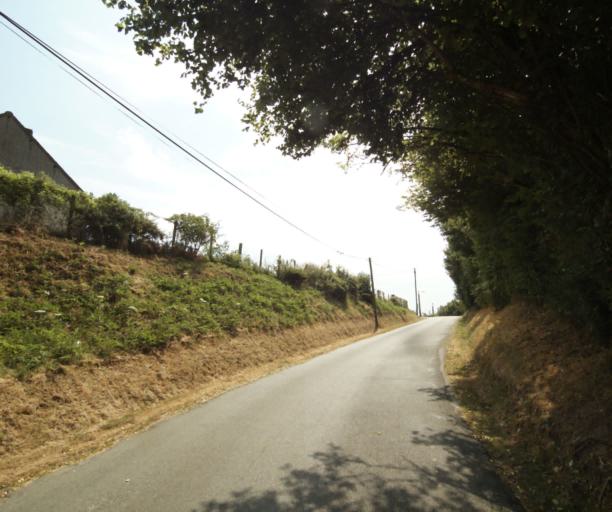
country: FR
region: Centre
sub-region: Departement d'Eure-et-Loir
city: Authon-du-Perche
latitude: 48.1924
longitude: 0.9369
